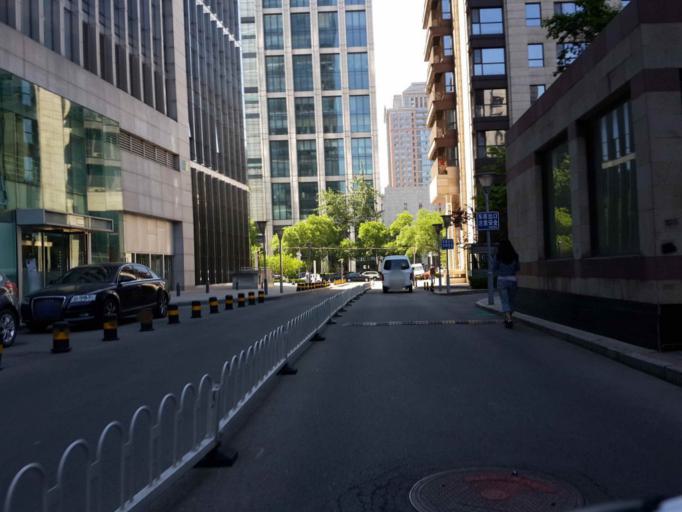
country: CN
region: Beijing
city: Chaowai
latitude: 39.9282
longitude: 116.4537
